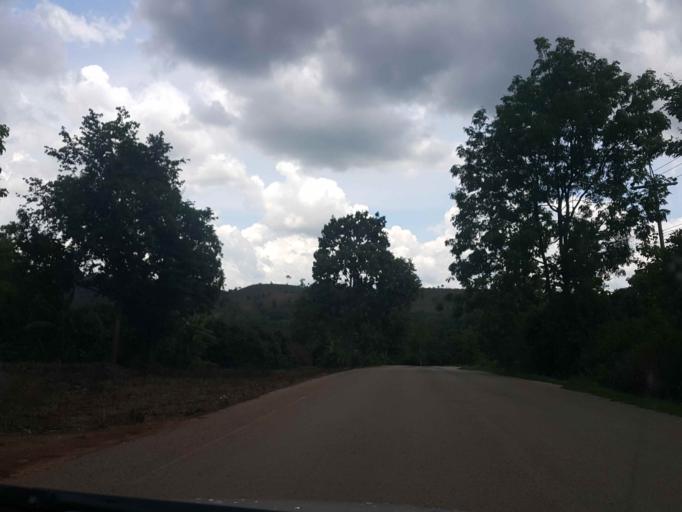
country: TH
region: Phayao
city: Dok Kham Tai
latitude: 18.9700
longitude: 100.0745
